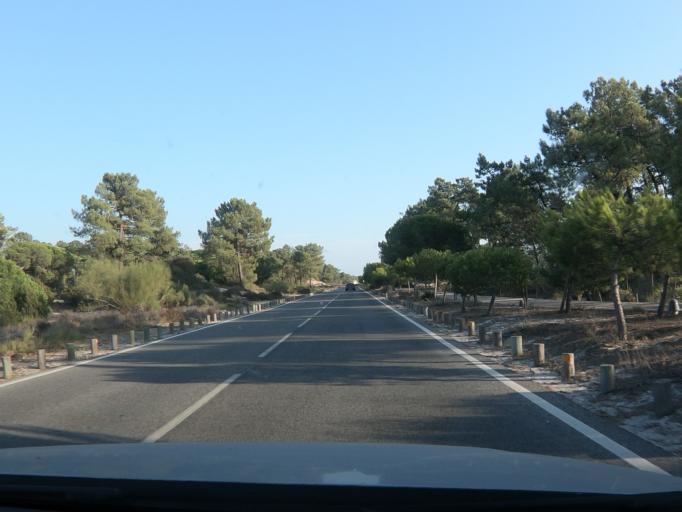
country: PT
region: Setubal
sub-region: Setubal
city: Setubal
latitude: 38.4842
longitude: -8.8936
